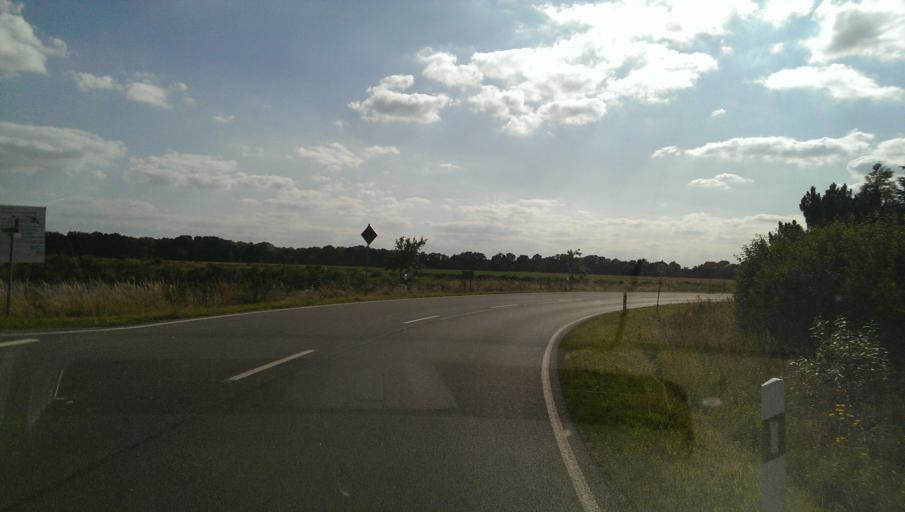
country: DE
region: Saxony
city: Bad Duben
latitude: 51.5888
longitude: 12.5457
